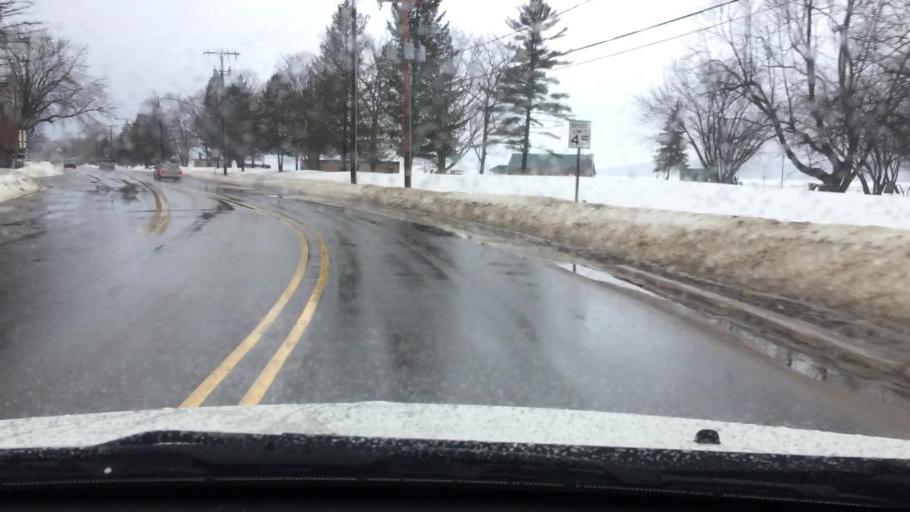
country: US
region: Michigan
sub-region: Charlevoix County
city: East Jordan
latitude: 45.1548
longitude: -85.1402
